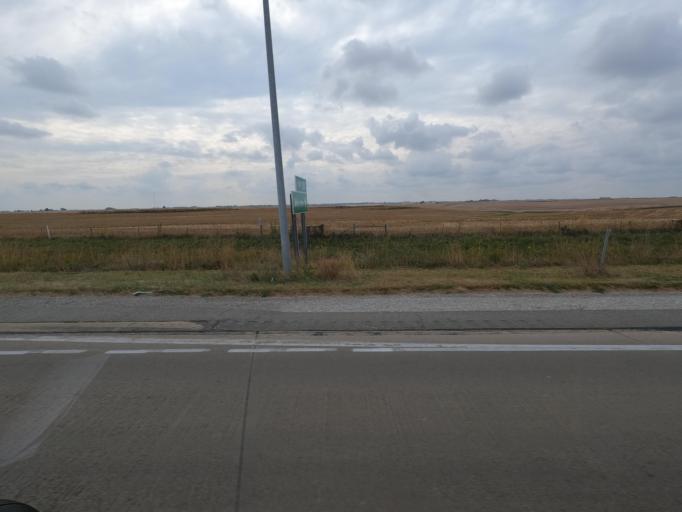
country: US
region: Iowa
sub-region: Jasper County
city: Monroe
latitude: 41.5501
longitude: -93.1352
